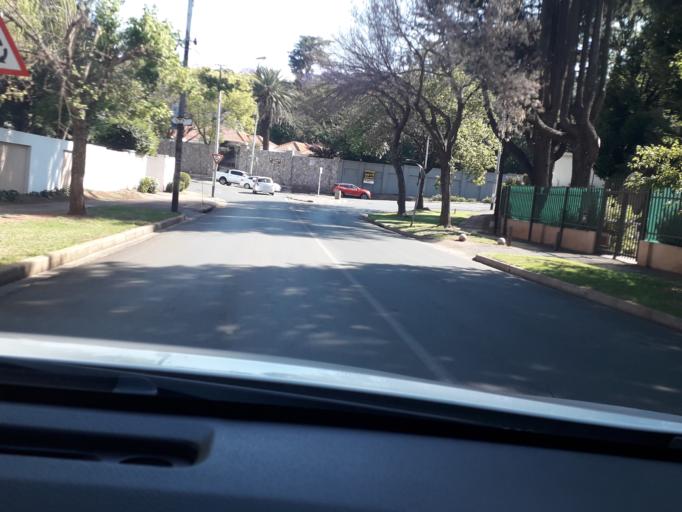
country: ZA
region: Gauteng
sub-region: City of Johannesburg Metropolitan Municipality
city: Johannesburg
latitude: -26.1794
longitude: 28.0213
